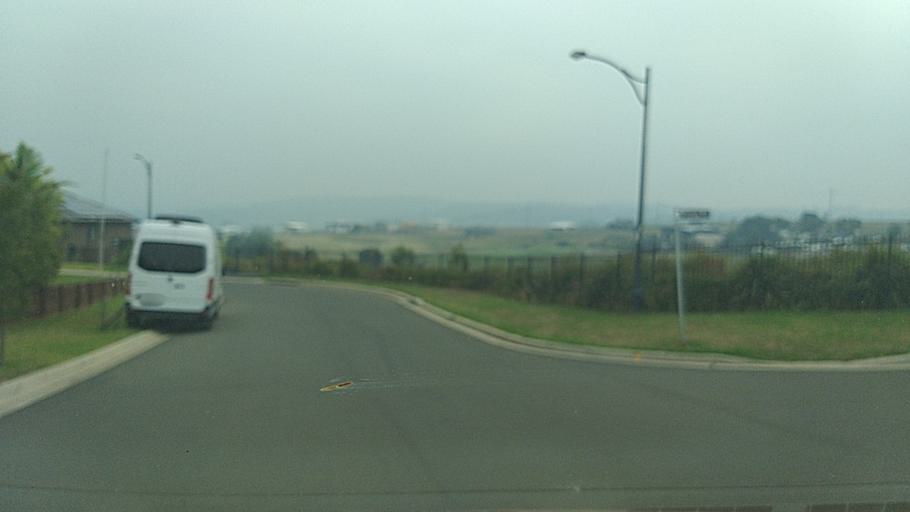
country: AU
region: New South Wales
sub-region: Shellharbour
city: Croom
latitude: -34.5983
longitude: 150.8523
